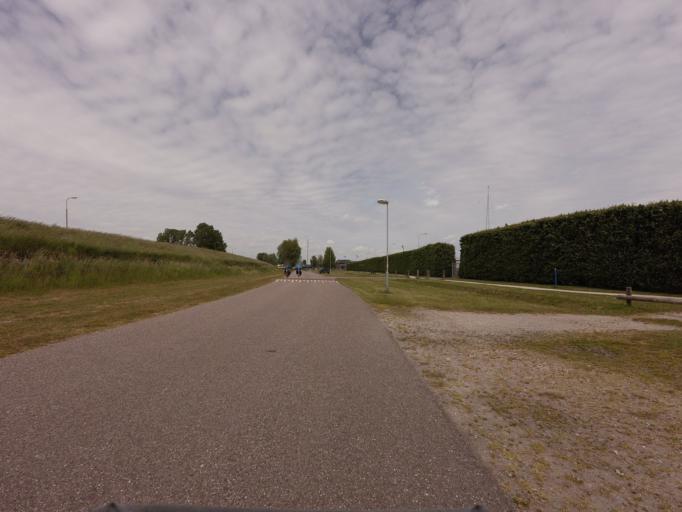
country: NL
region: North Holland
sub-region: Gemeente Medemblik
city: Medemblik
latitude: 52.7674
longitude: 5.1172
